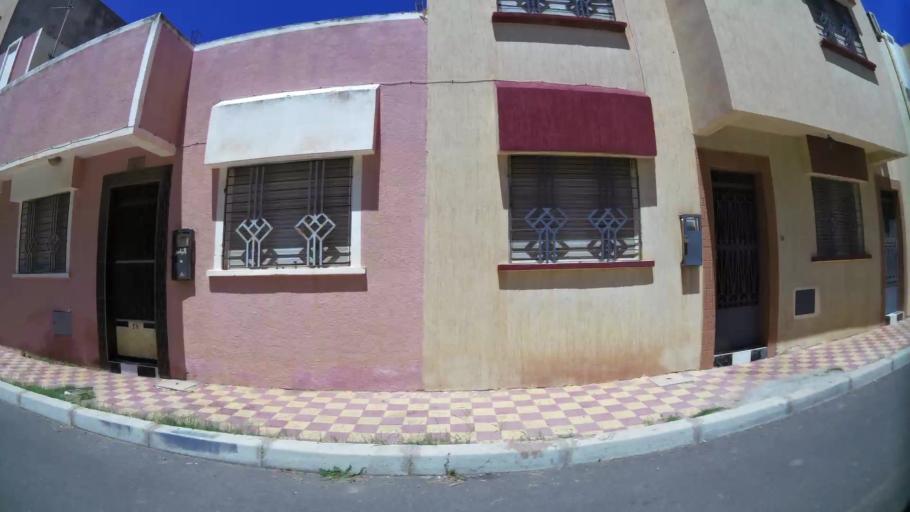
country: MA
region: Oriental
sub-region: Berkane-Taourirt
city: Madagh
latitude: 35.0762
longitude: -2.2183
